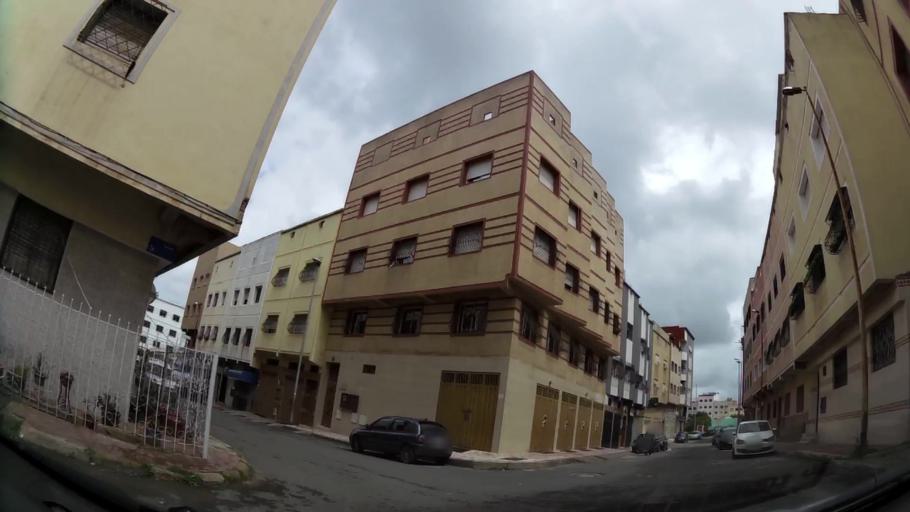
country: MA
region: Grand Casablanca
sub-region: Casablanca
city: Casablanca
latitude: 33.5335
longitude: -7.5900
